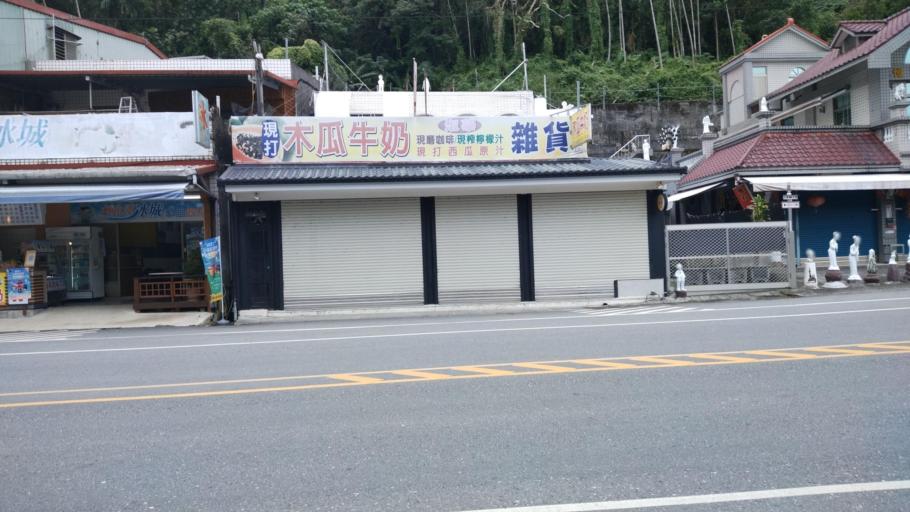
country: TW
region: Taiwan
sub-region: Hualien
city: Hualian
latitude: 23.9278
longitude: 121.5057
